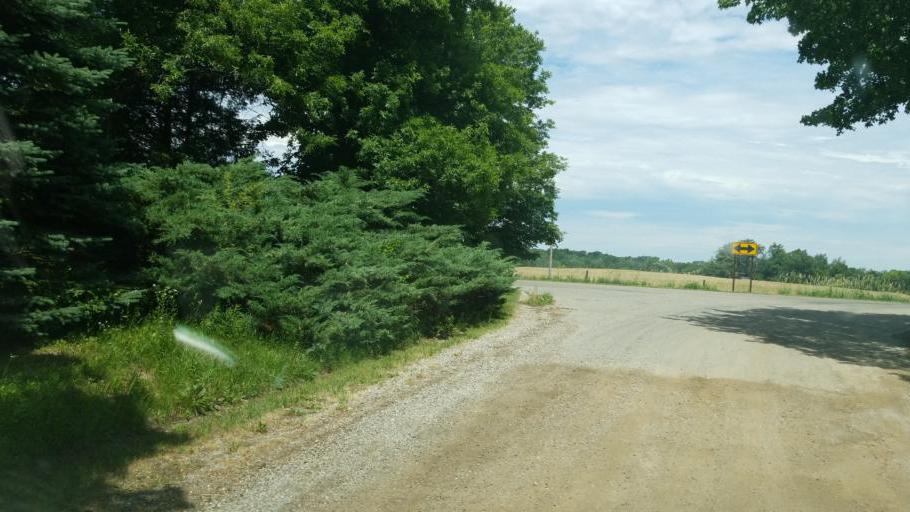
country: US
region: Michigan
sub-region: Eaton County
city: Charlotte
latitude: 42.6258
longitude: -84.8855
